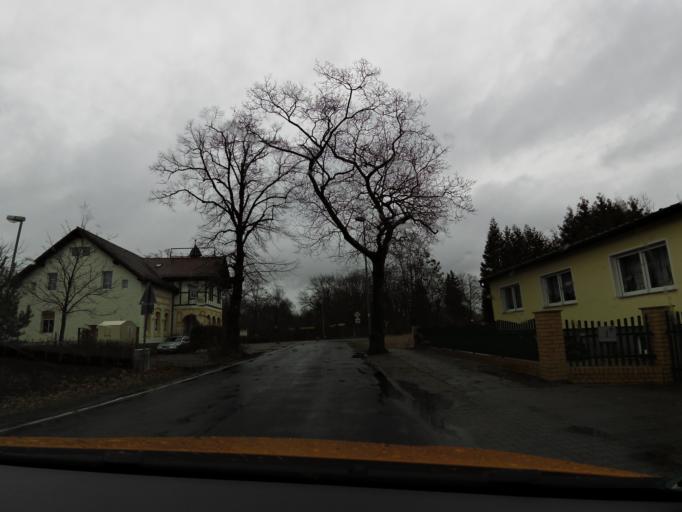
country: DE
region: Brandenburg
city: Am Mellensee
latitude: 52.1838
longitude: 13.4027
